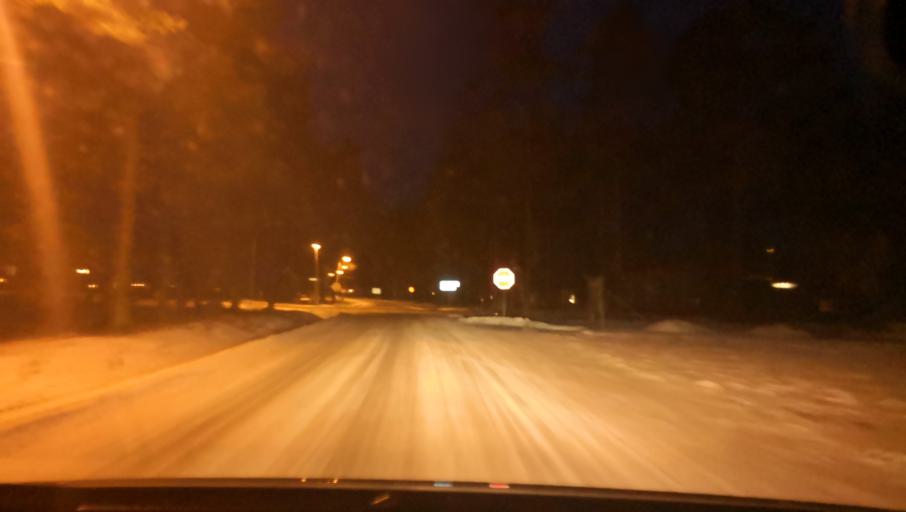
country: SE
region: Uppsala
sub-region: Heby Kommun
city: Tarnsjo
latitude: 60.2998
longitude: 16.8062
